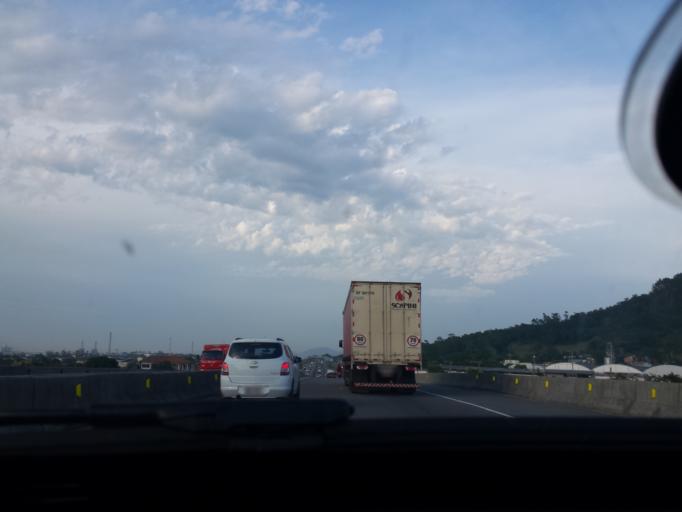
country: BR
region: Santa Catarina
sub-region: Tubarao
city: Tubarao
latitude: -28.4254
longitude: -48.9435
